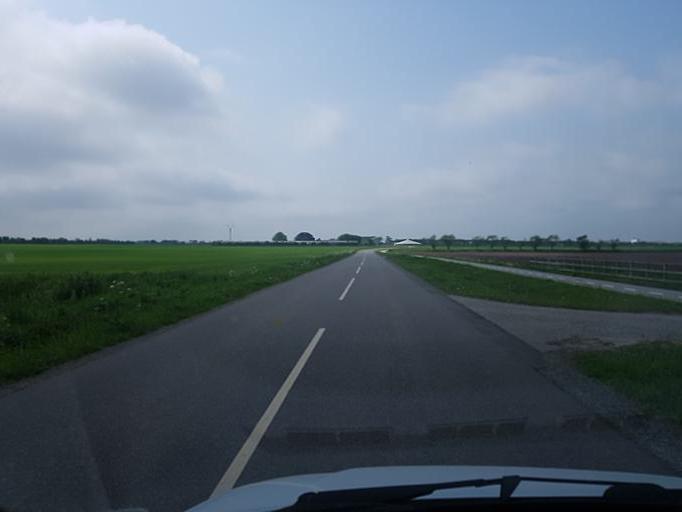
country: DK
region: South Denmark
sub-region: Varde Kommune
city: Varde
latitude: 55.5399
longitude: 8.5004
